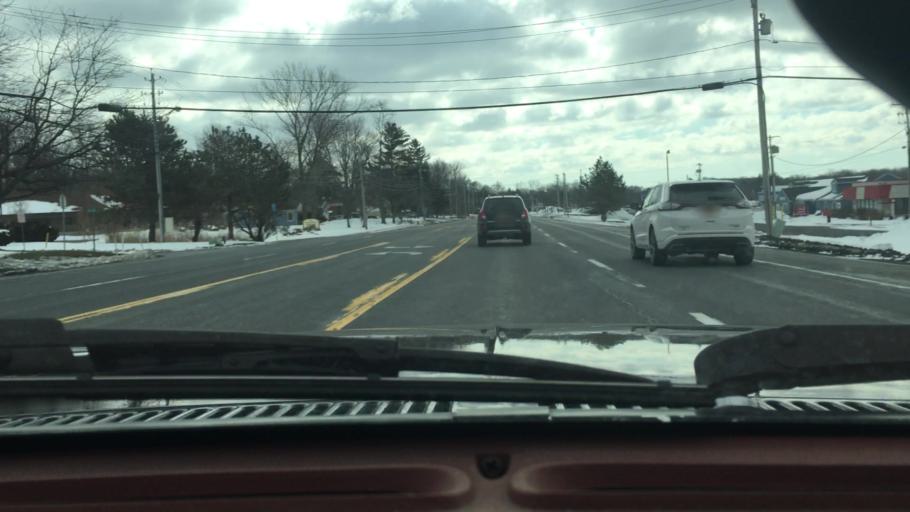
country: US
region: New York
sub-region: Onondaga County
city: Liverpool
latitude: 43.1620
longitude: -76.2335
